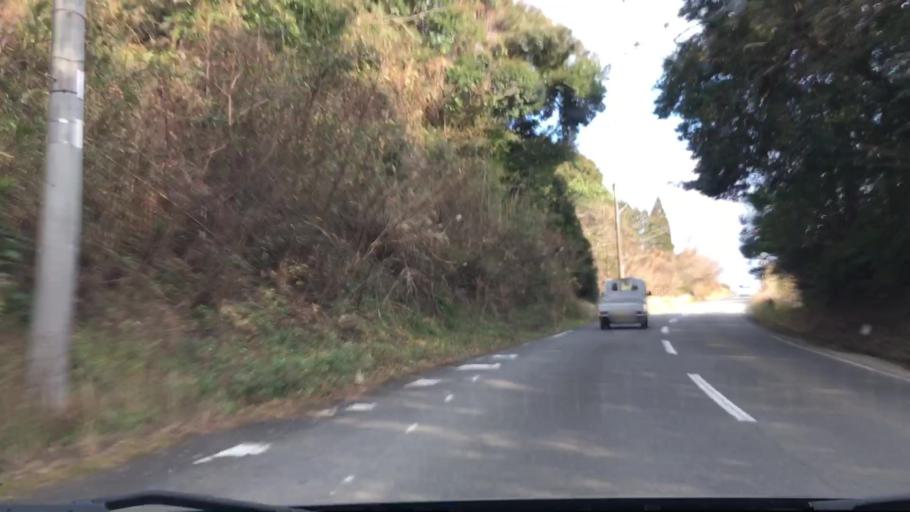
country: JP
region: Miyazaki
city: Nichinan
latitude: 31.5995
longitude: 131.3189
